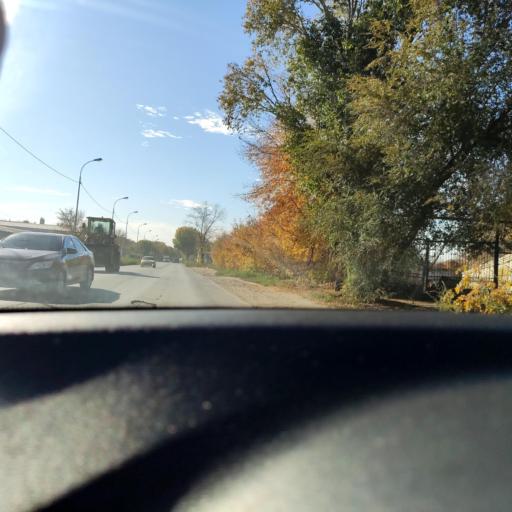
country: RU
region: Samara
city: Petra-Dubrava
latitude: 53.2415
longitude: 50.2972
